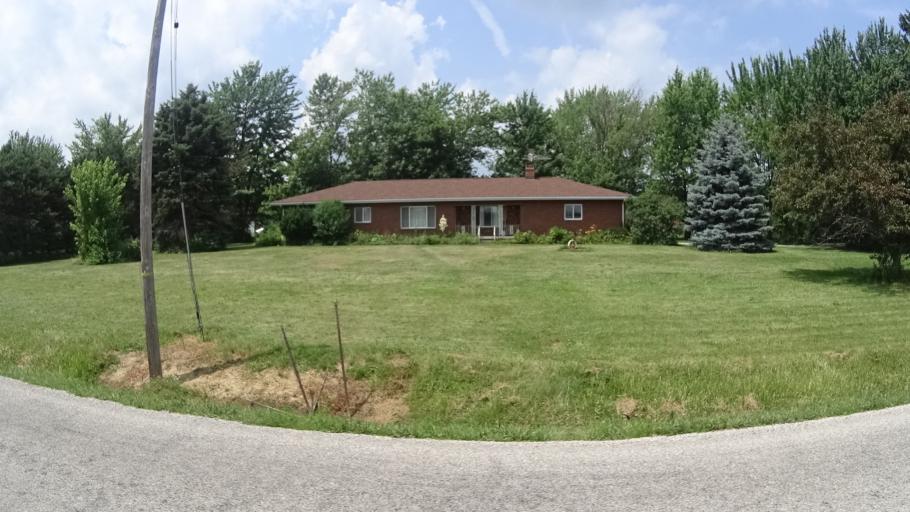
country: US
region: Ohio
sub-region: Lorain County
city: Vermilion
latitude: 41.4002
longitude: -82.3901
